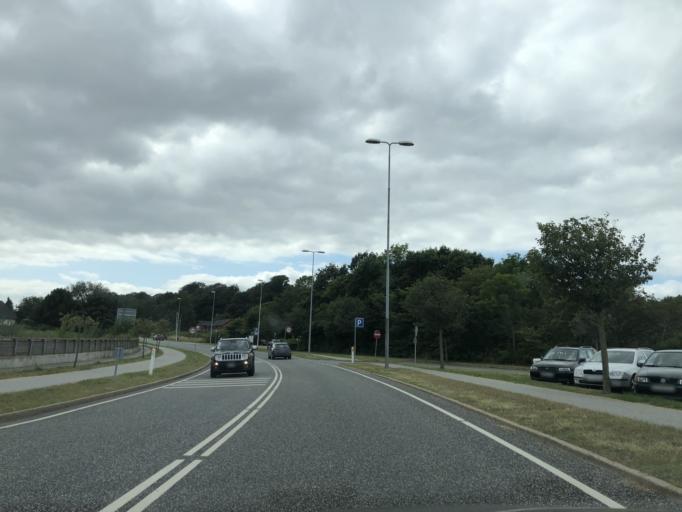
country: DK
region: South Denmark
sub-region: Sonderborg Kommune
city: Guderup
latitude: 54.9934
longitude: 9.9829
